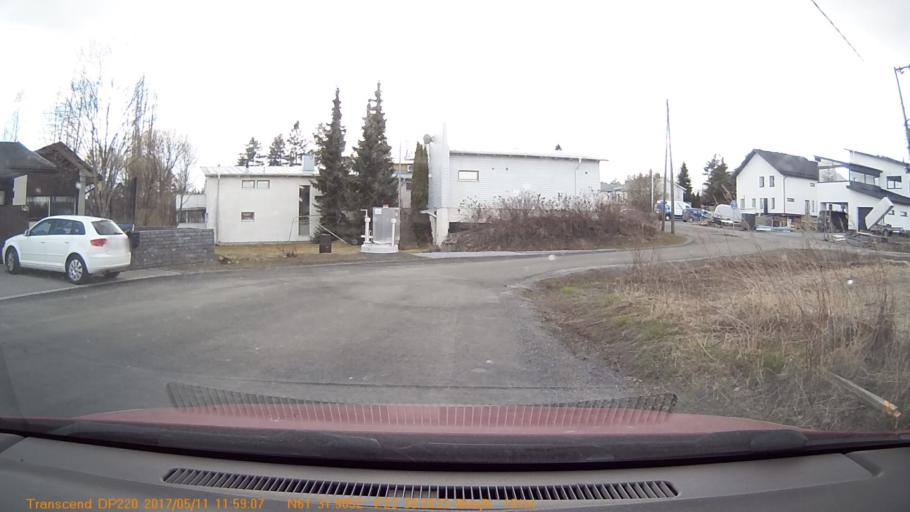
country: FI
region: Pirkanmaa
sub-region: Tampere
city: Yloejaervi
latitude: 61.5331
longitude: 23.6544
